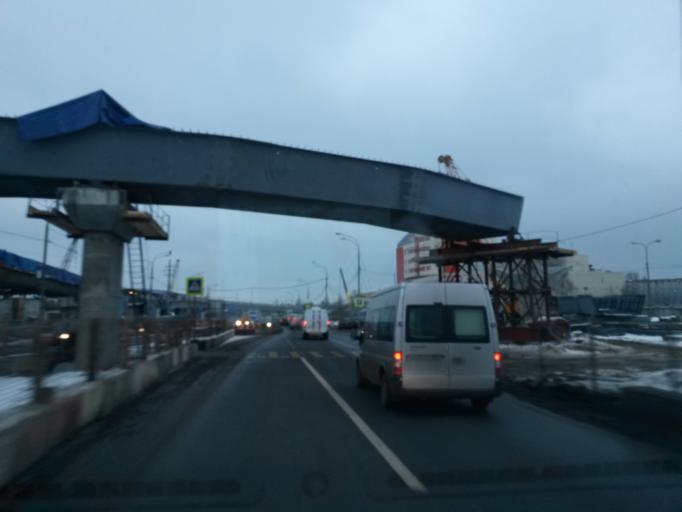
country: RU
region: Moskovskaya
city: Bol'shaya Setun'
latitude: 55.7000
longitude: 37.4218
